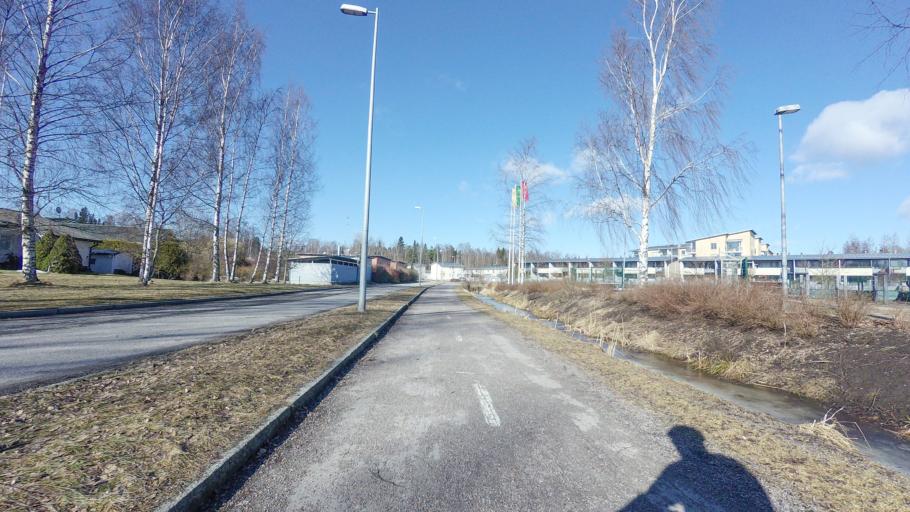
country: FI
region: Uusimaa
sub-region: Helsinki
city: Helsinki
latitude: 60.1751
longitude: 25.0540
